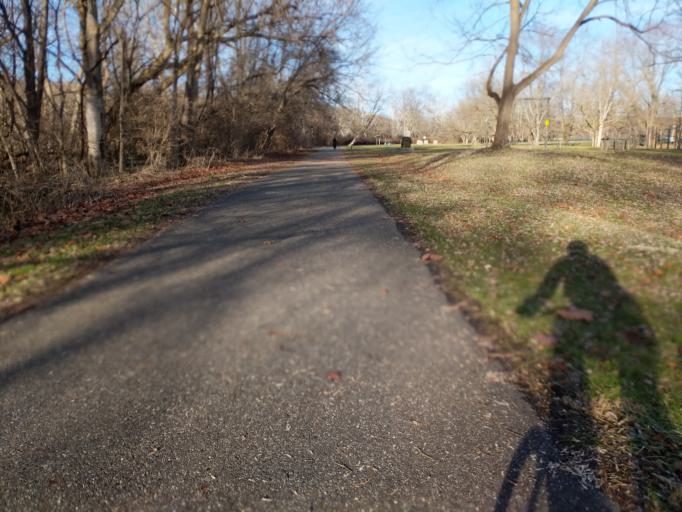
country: US
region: Ohio
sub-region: Athens County
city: Athens
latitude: 39.3344
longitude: -82.1249
